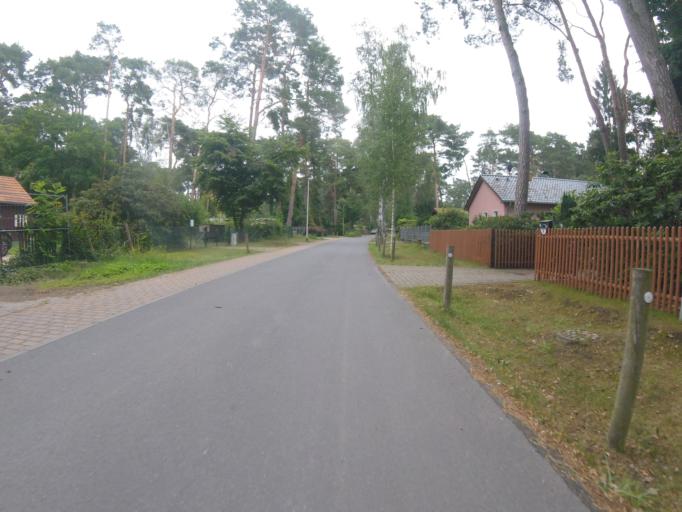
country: DE
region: Brandenburg
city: Bestensee
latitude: 52.2908
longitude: 13.7079
